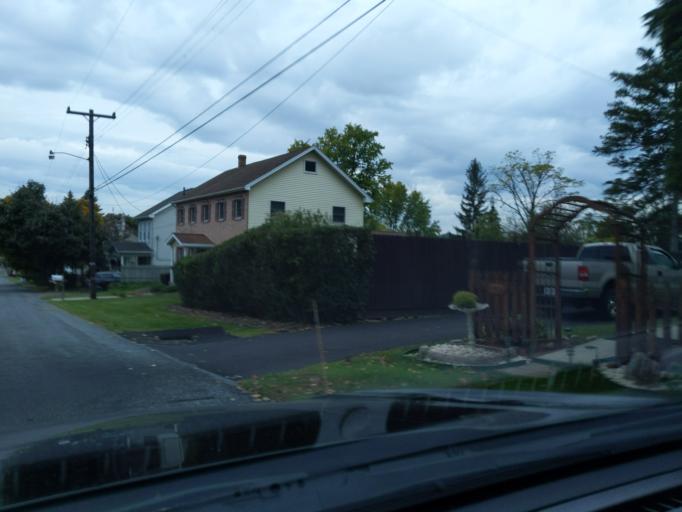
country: US
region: Pennsylvania
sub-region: Blair County
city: Altoona
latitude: 40.5042
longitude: -78.3810
